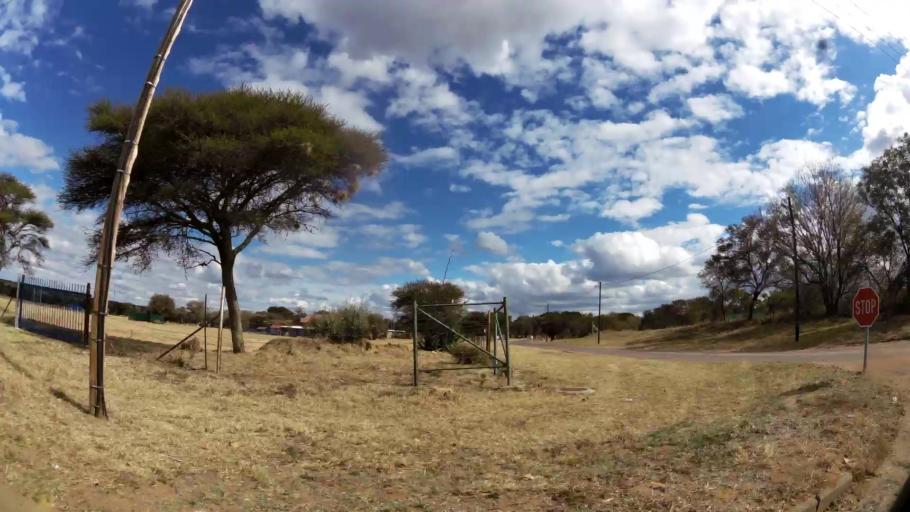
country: ZA
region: Limpopo
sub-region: Waterberg District Municipality
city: Modimolle
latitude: -24.7103
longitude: 28.4016
